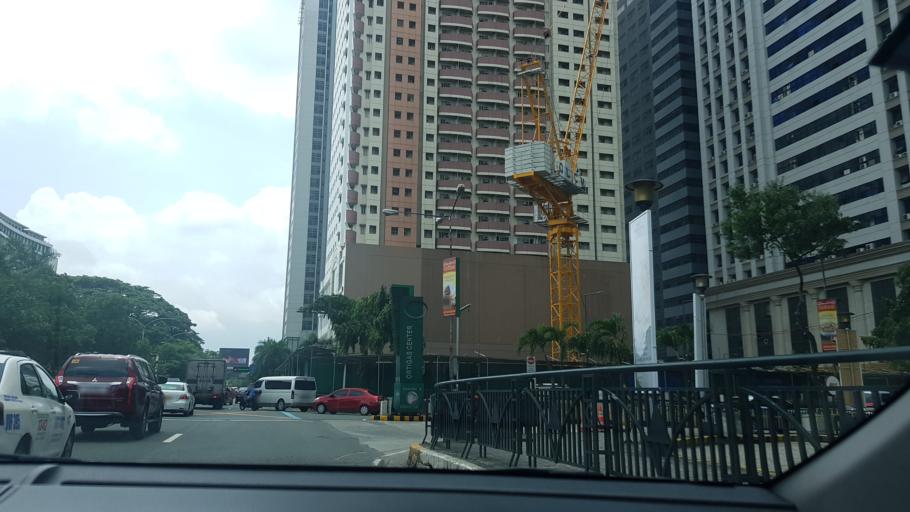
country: PH
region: Metro Manila
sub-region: Pasig
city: Pasig City
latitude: 14.5908
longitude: 121.0610
